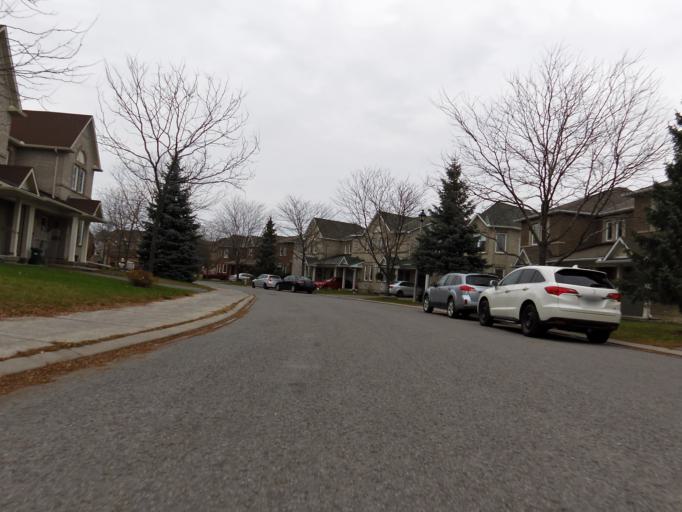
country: CA
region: Ontario
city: Bells Corners
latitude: 45.2738
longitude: -75.7074
